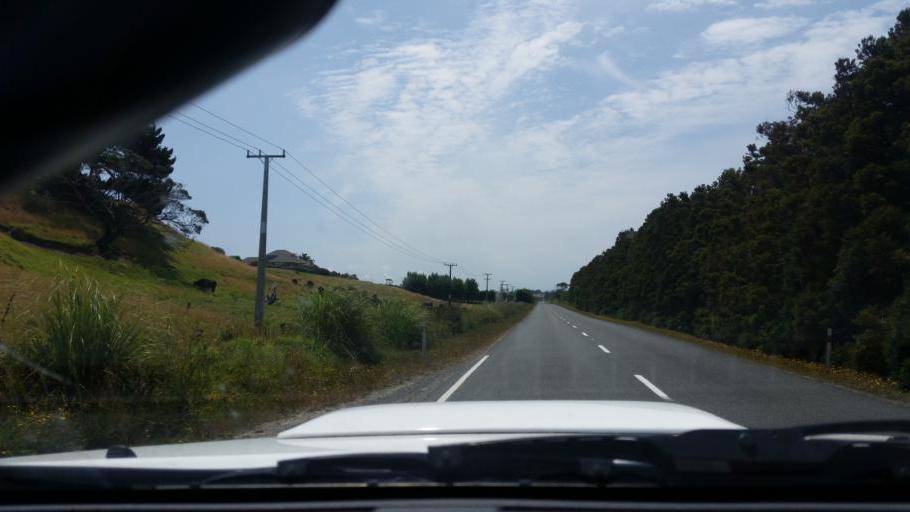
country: NZ
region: Northland
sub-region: Kaipara District
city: Dargaville
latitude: -36.0594
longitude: 173.9352
